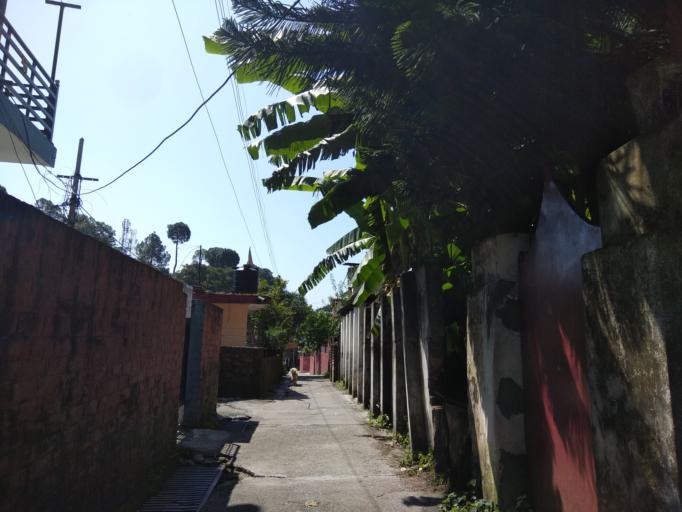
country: IN
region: Himachal Pradesh
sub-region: Kangra
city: Palampur
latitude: 32.1214
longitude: 76.5396
